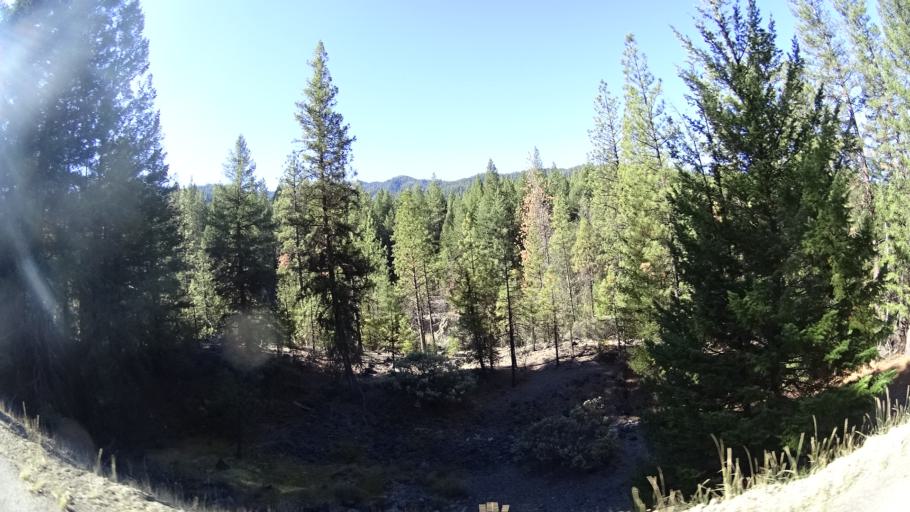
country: US
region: California
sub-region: Trinity County
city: Weaverville
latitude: 41.1155
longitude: -123.0903
